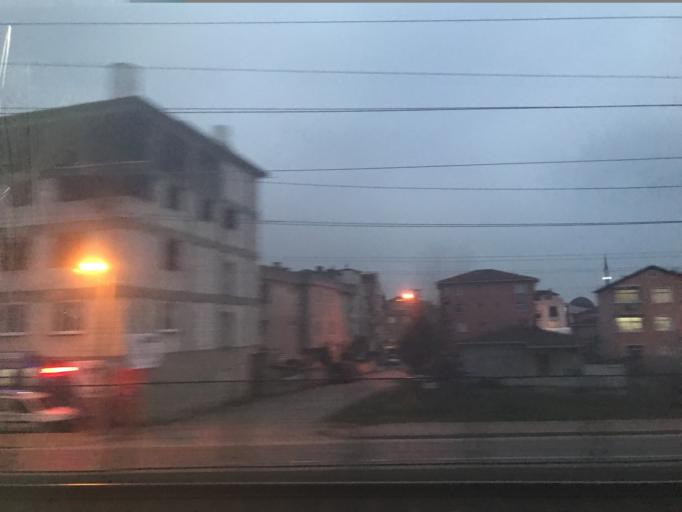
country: TR
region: Kocaeli
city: Darica
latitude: 40.7881
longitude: 29.3975
